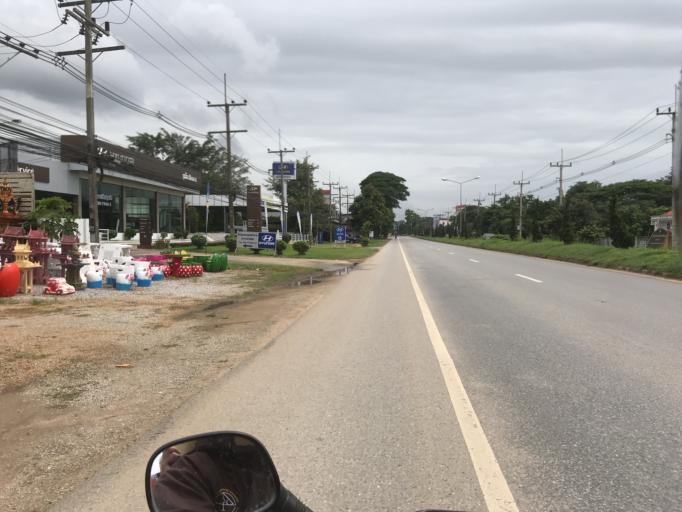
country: TH
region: Chiang Rai
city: Chiang Rai
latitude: 19.9442
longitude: 99.8469
